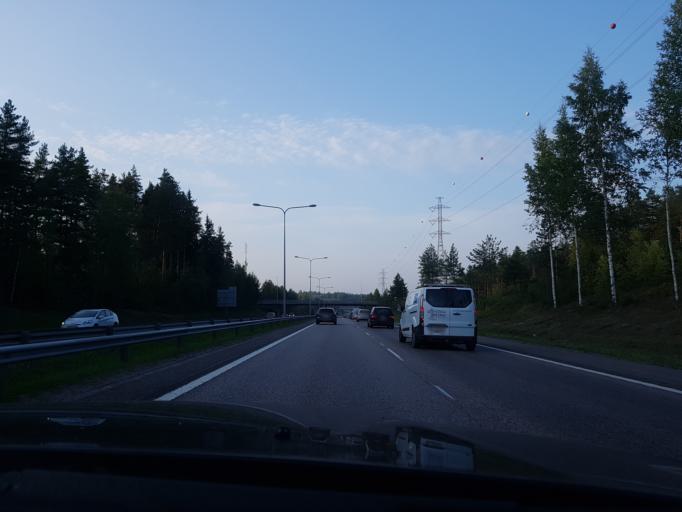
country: FI
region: Uusimaa
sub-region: Helsinki
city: Vantaa
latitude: 60.3154
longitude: 24.9976
